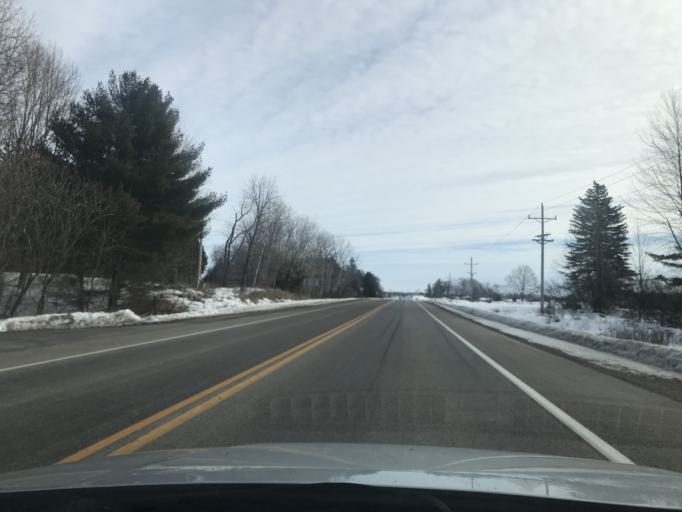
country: US
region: Wisconsin
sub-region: Oconto County
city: Oconto Falls
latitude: 44.8868
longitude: -88.1622
